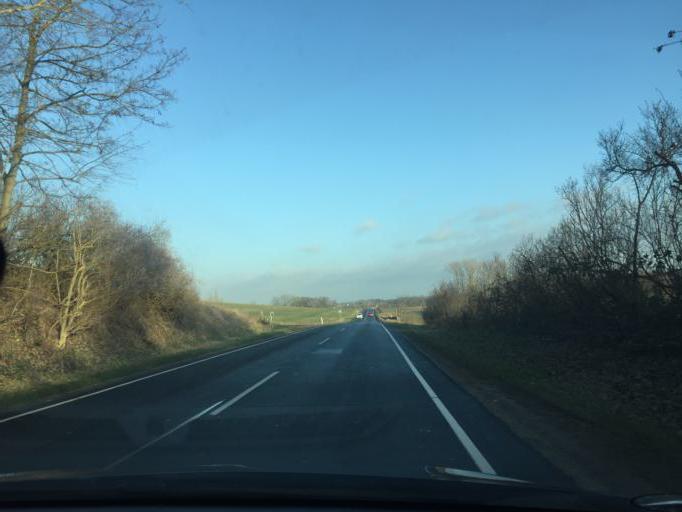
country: DK
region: South Denmark
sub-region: Faaborg-Midtfyn Kommune
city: Faaborg
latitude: 55.1699
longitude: 10.2829
